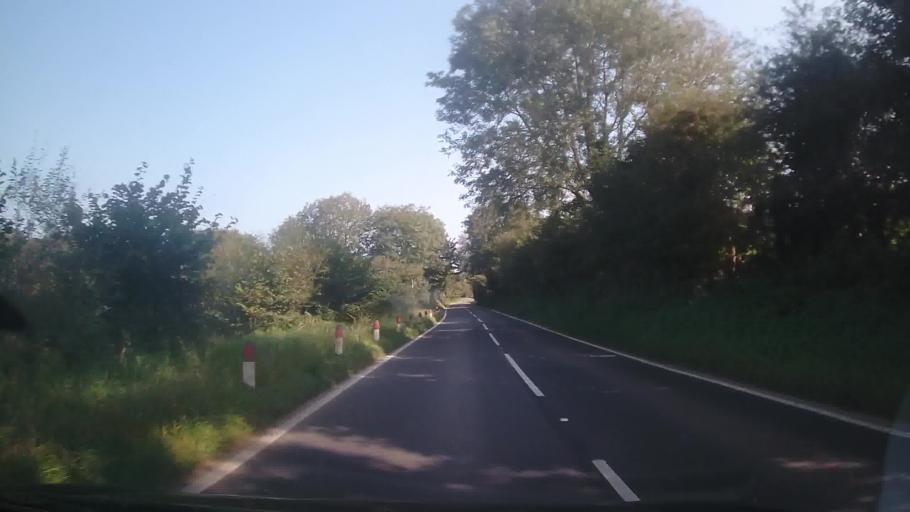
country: GB
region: Wales
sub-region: Pembrokeshire
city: Nevern
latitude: 52.0164
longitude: -4.7866
